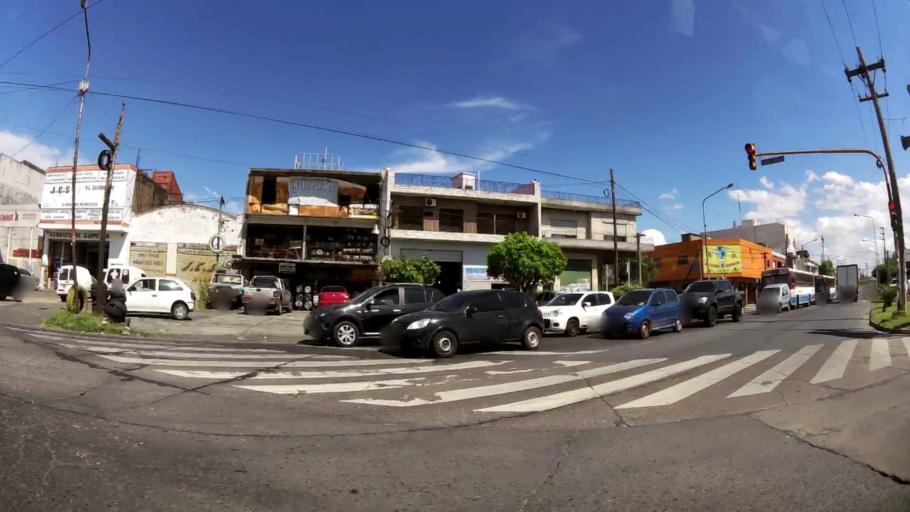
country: AR
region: Buenos Aires
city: San Justo
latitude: -34.6672
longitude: -58.5513
